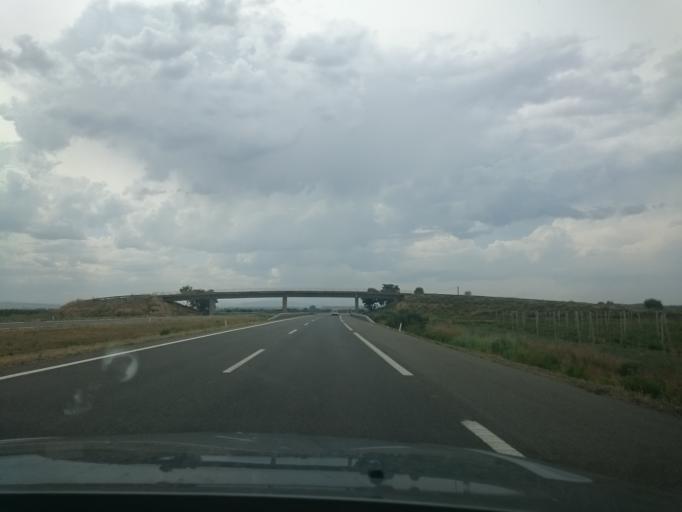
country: ES
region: Navarre
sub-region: Provincia de Navarra
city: Fontellas
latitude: 42.0176
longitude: -1.6129
